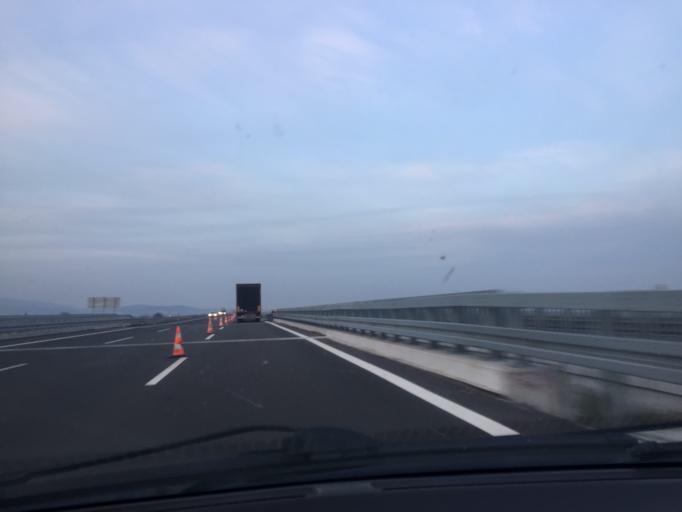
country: TR
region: Manisa
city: Halitpasa
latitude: 38.7292
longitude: 27.6549
